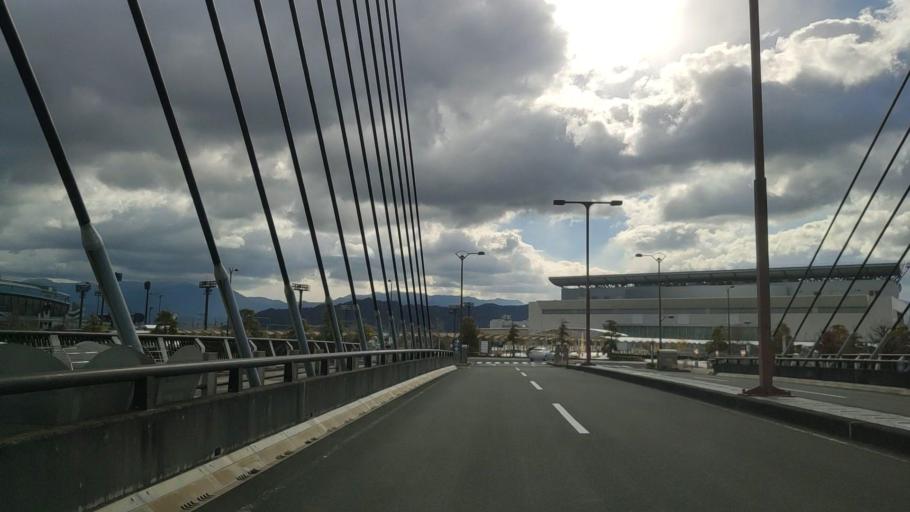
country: JP
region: Ehime
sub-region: Shikoku-chuo Shi
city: Matsuyama
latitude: 33.8106
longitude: 132.7419
